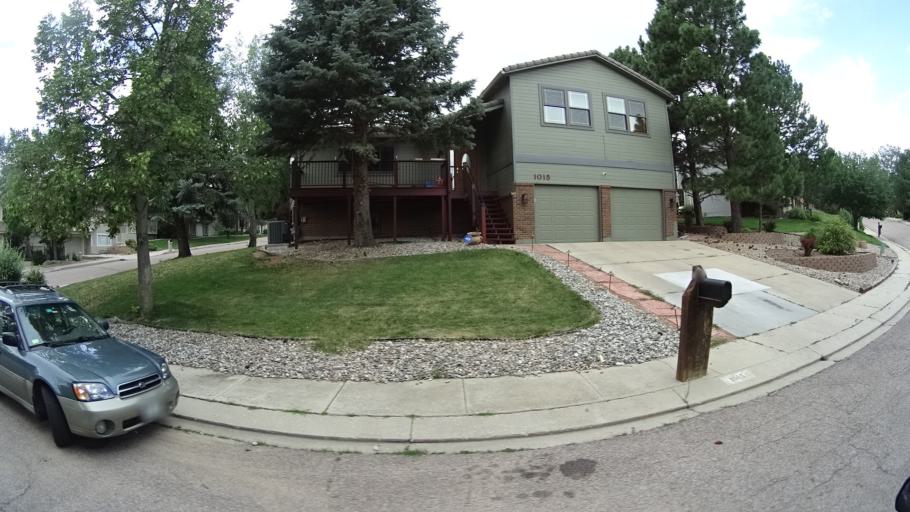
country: US
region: Colorado
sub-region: El Paso County
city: Colorado Springs
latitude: 38.9106
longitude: -104.8459
